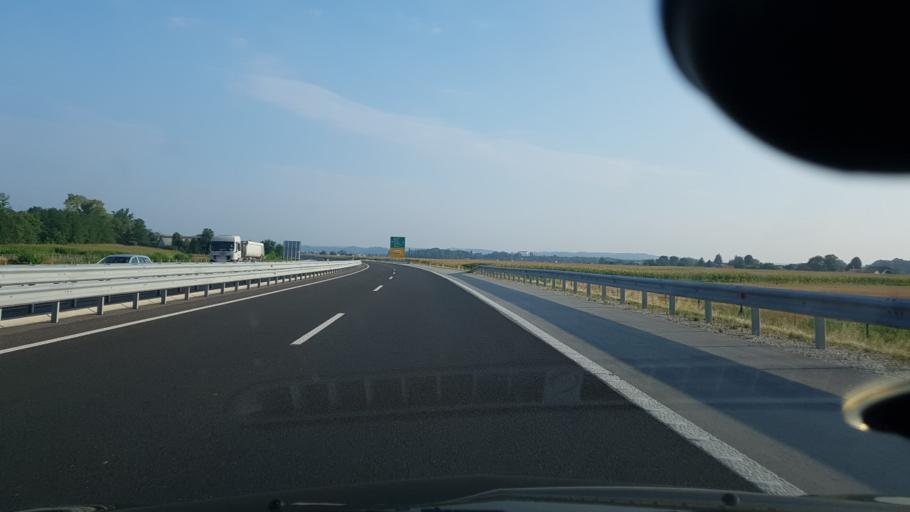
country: SI
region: Hajdina
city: Spodnja Hajdina
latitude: 46.3815
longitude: 15.8661
